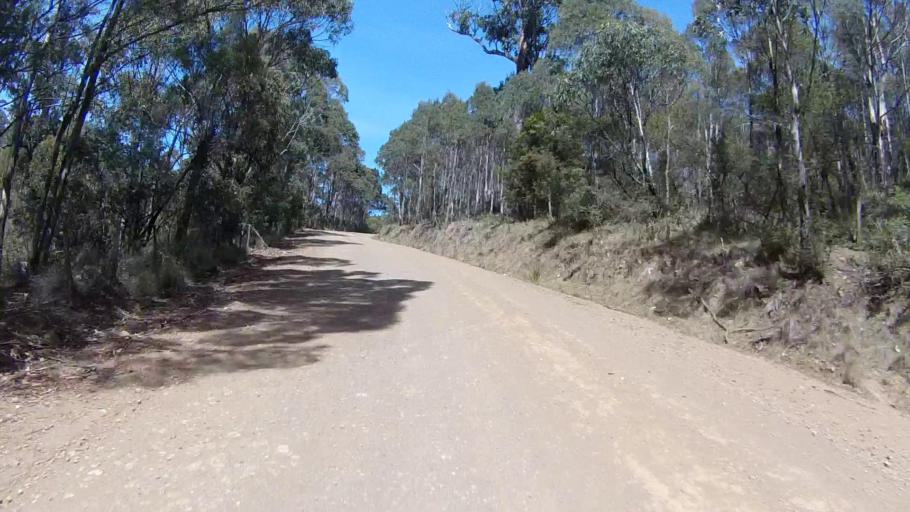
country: AU
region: Tasmania
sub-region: Sorell
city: Sorell
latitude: -42.6539
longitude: 147.7412
